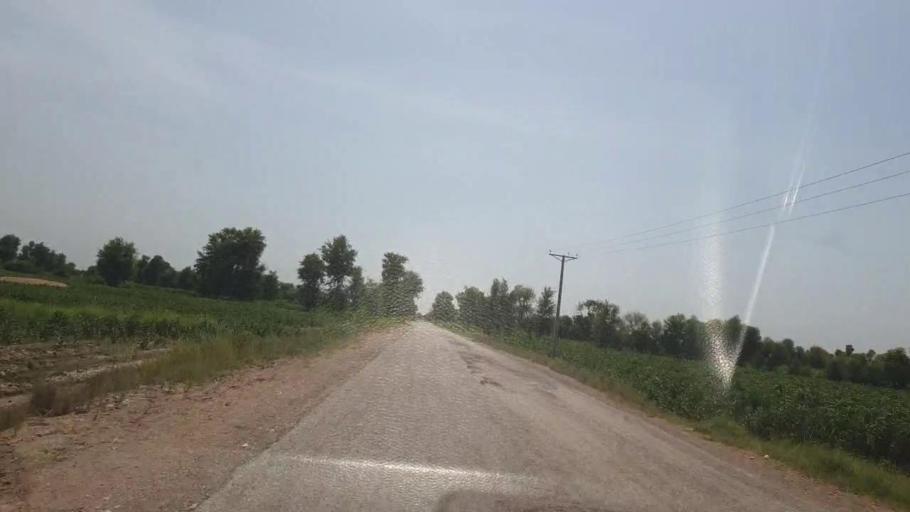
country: PK
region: Sindh
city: Kandiari
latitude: 27.0537
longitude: 68.5542
